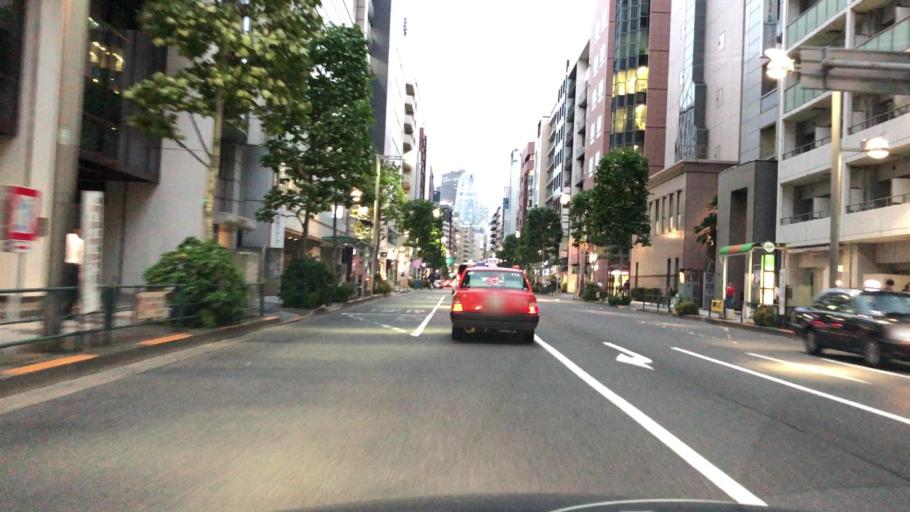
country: JP
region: Tokyo
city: Tokyo
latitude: 35.6879
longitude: 139.7136
